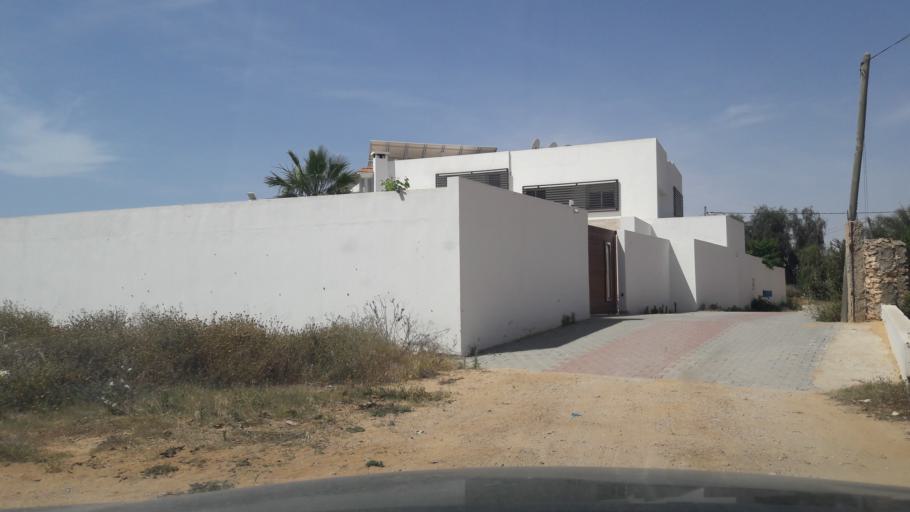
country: TN
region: Safaqis
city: Al Qarmadah
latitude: 34.7873
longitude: 10.7591
